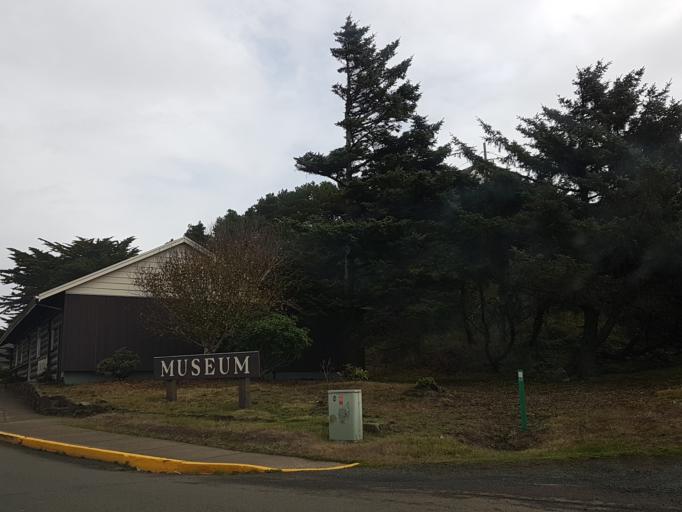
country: US
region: Oregon
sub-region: Lincoln County
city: Newport
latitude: 44.6309
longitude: -124.0591
